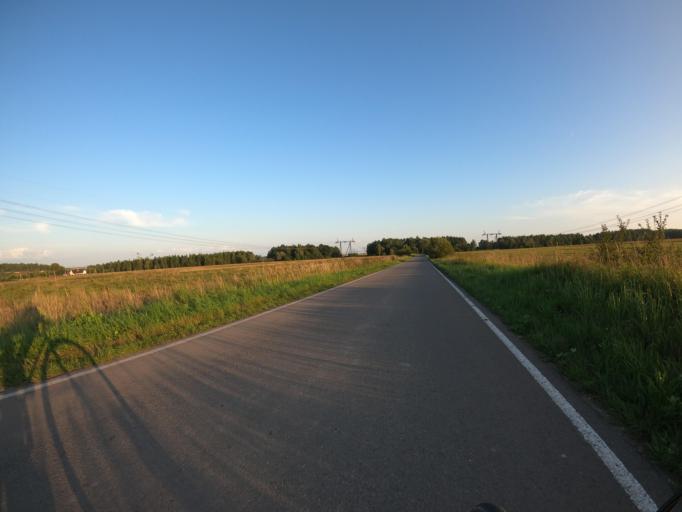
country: RU
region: Moskovskaya
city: Malino
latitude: 55.0984
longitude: 38.2856
